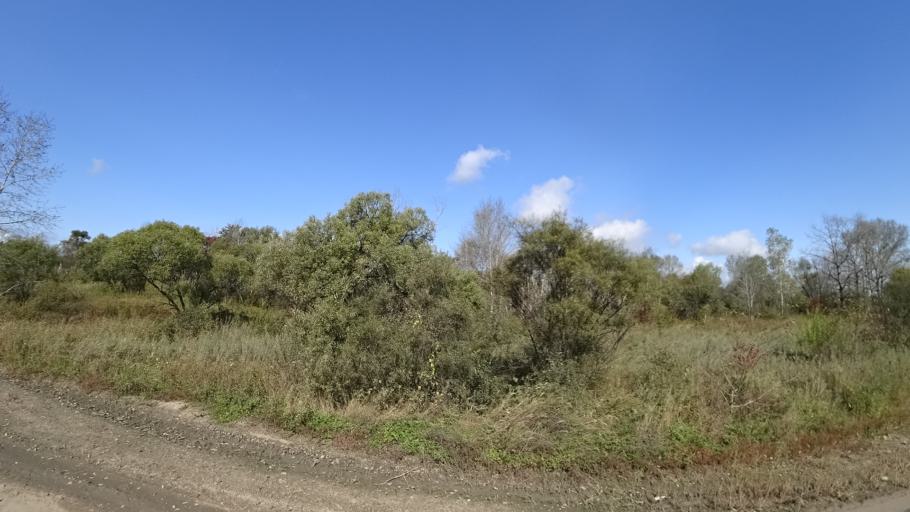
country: RU
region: Amur
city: Arkhara
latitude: 49.4073
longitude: 130.1590
